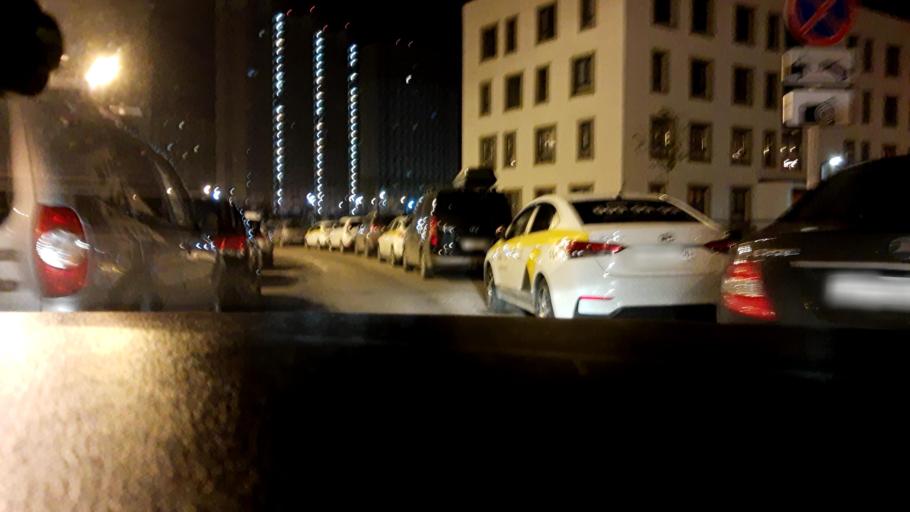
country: RU
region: Moscow
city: Khimki
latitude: 55.8744
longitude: 37.3974
